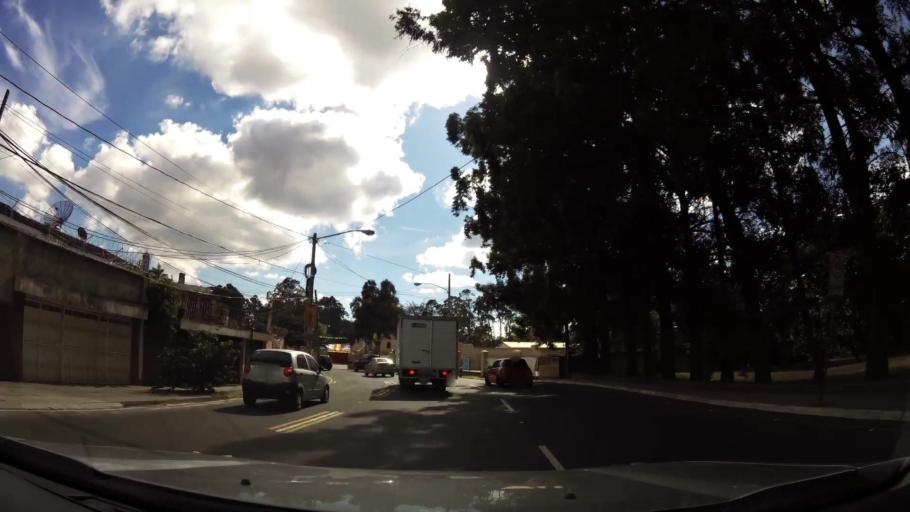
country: GT
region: Guatemala
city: Mixco
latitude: 14.5983
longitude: -90.5643
